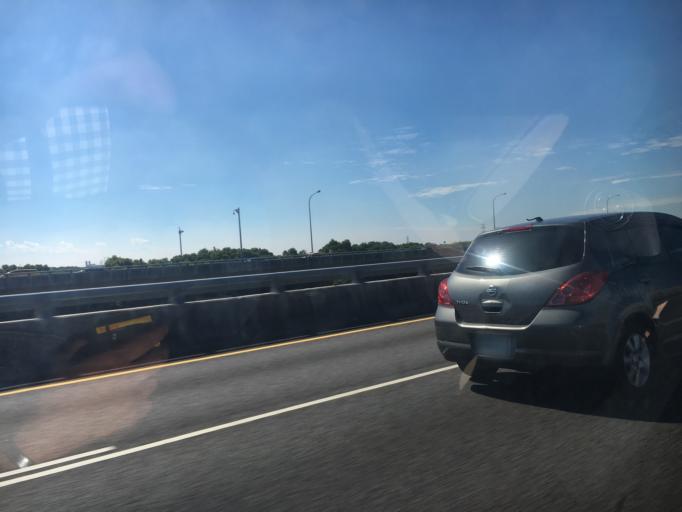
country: TW
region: Taiwan
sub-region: Taoyuan
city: Taoyuan
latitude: 25.0659
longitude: 121.3515
